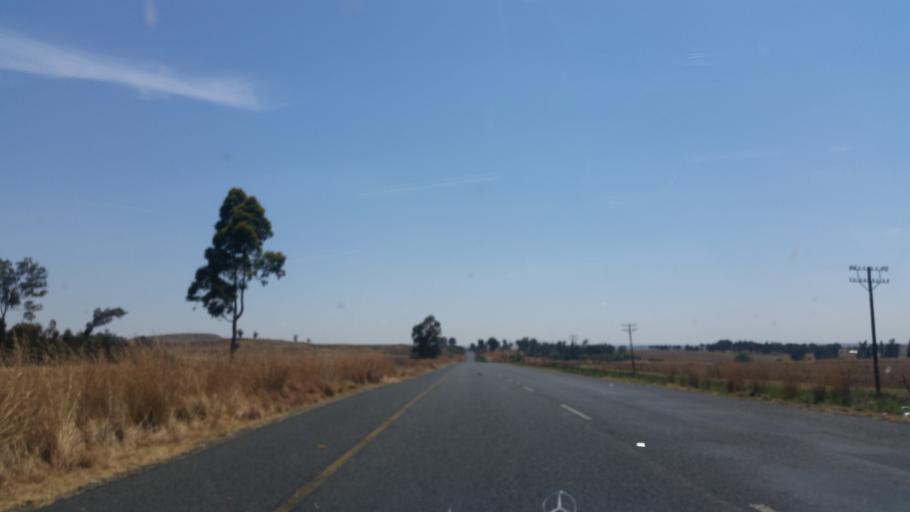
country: ZA
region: Orange Free State
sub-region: Thabo Mofutsanyana District Municipality
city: Phuthaditjhaba
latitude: -28.2375
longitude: 28.7077
